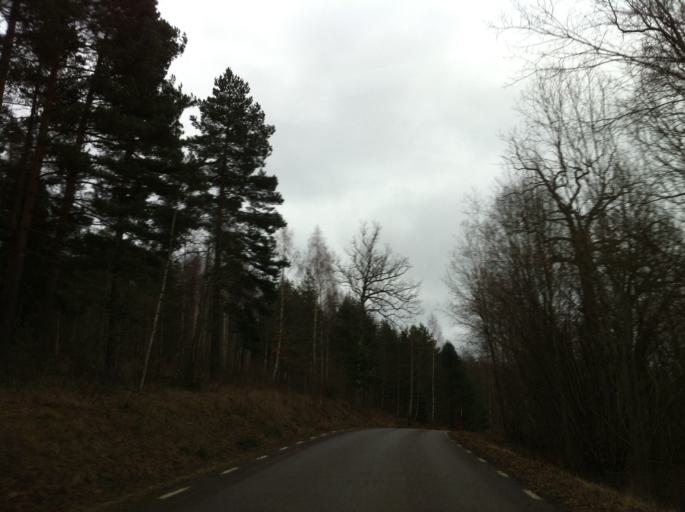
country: SE
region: Kalmar
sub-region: Vasterviks Kommun
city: Vaestervik
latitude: 57.9079
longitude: 16.6627
